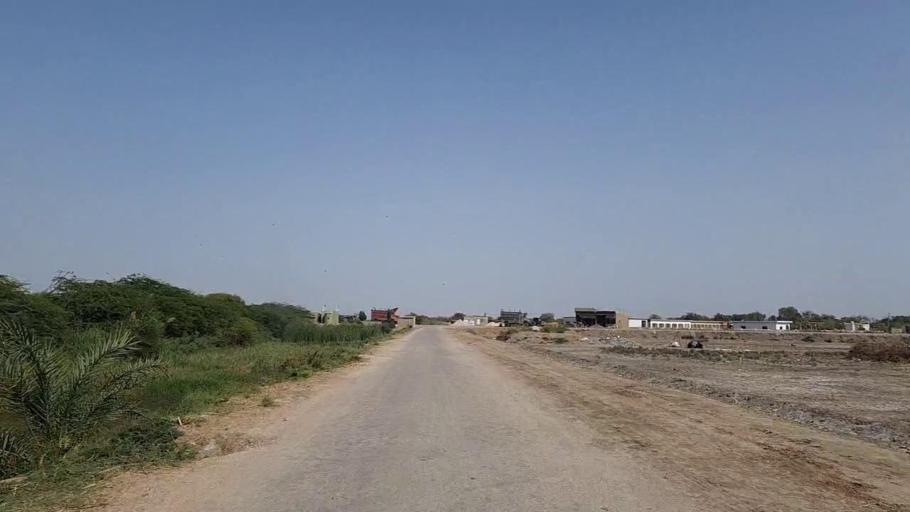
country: PK
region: Sindh
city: Jati
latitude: 24.3609
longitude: 68.2680
